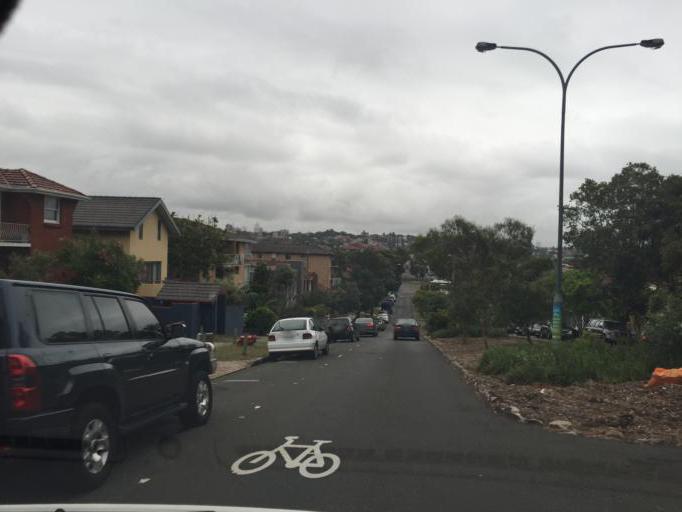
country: AU
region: New South Wales
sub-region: Waverley
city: North Bondi
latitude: -33.8859
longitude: 151.2832
